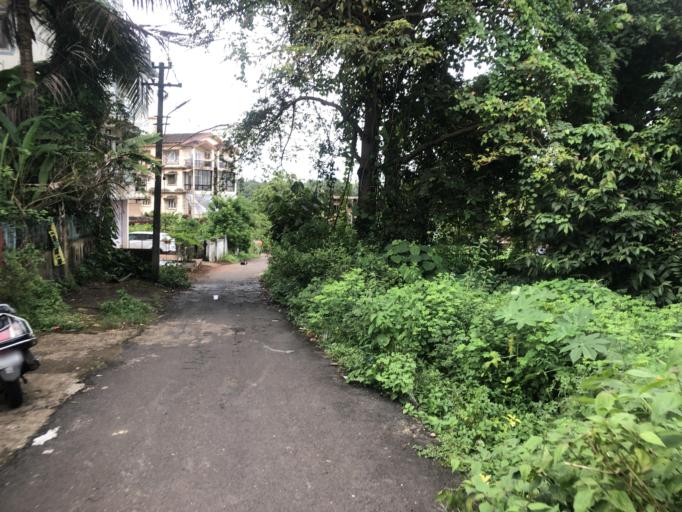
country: IN
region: Goa
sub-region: North Goa
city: Serula
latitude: 15.5473
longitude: 73.8237
